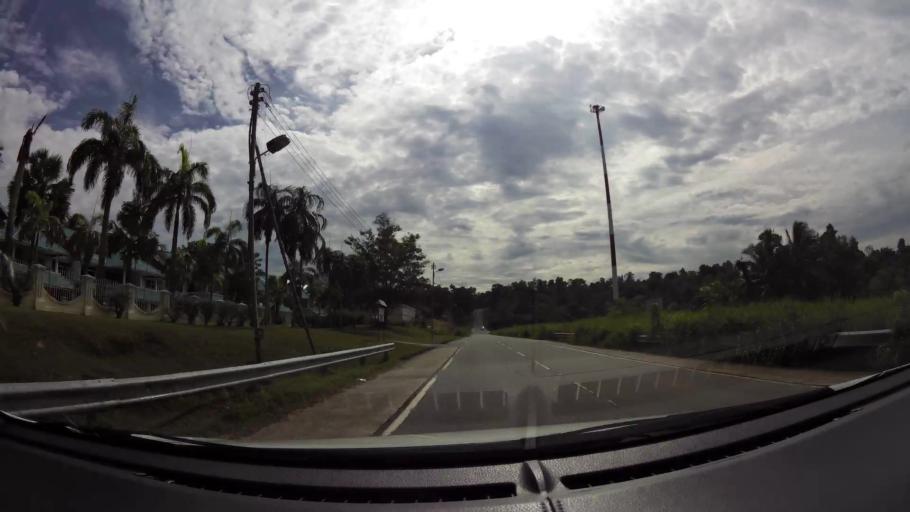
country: BN
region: Brunei and Muara
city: Bandar Seri Begawan
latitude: 4.8915
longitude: 114.8975
